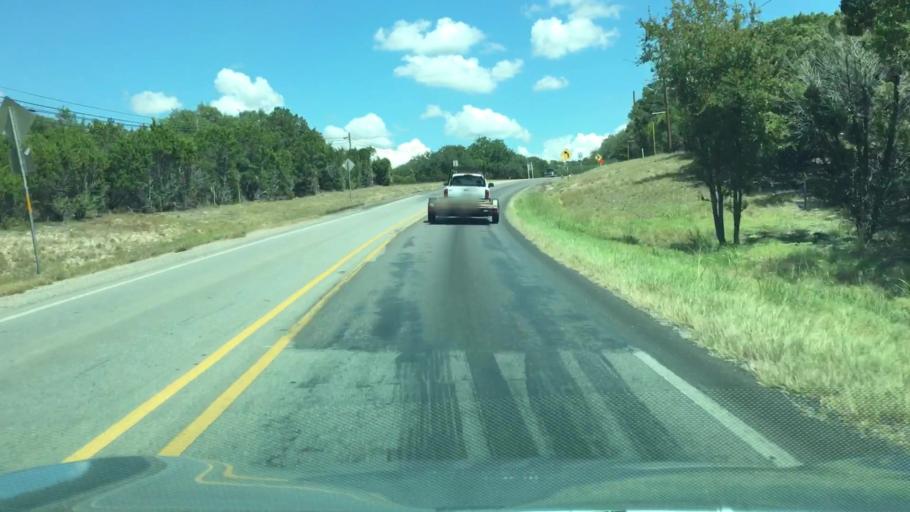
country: US
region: Texas
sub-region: Hays County
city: Wimberley
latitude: 29.9986
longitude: -98.0880
